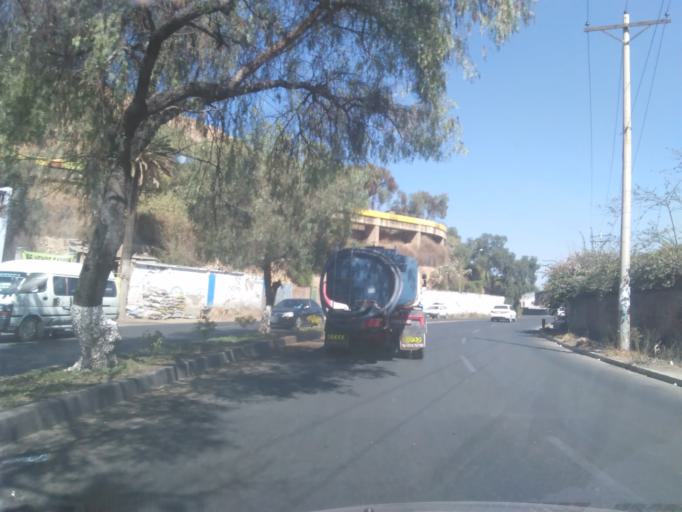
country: BO
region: Cochabamba
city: Cochabamba
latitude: -17.3814
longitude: -66.1420
